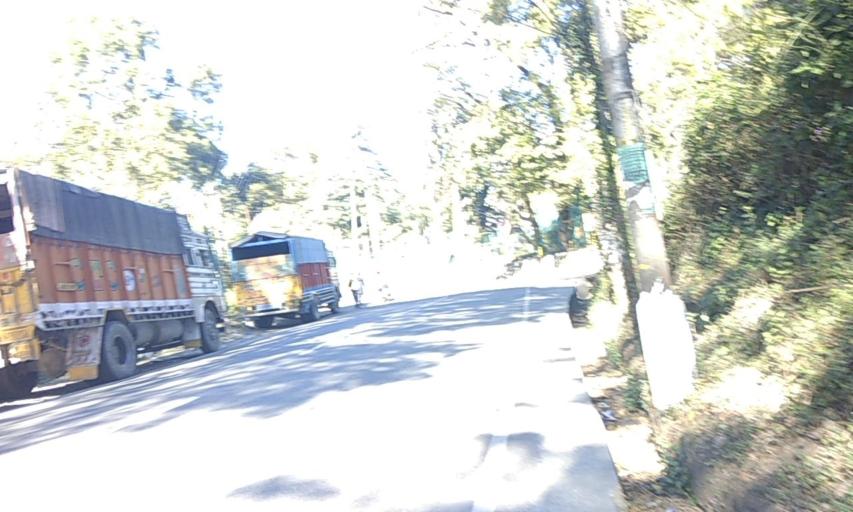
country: IN
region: Himachal Pradesh
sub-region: Kangra
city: Dharmsala
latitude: 32.2139
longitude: 76.3190
